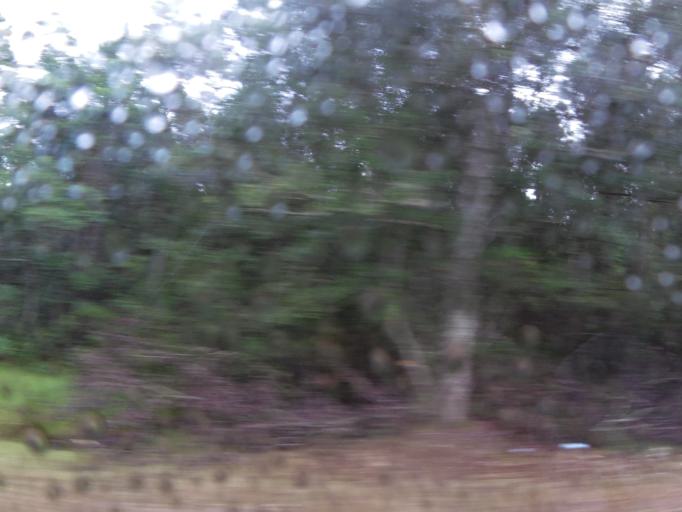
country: US
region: Florida
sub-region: Baker County
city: Macclenny
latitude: 30.4082
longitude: -82.1102
